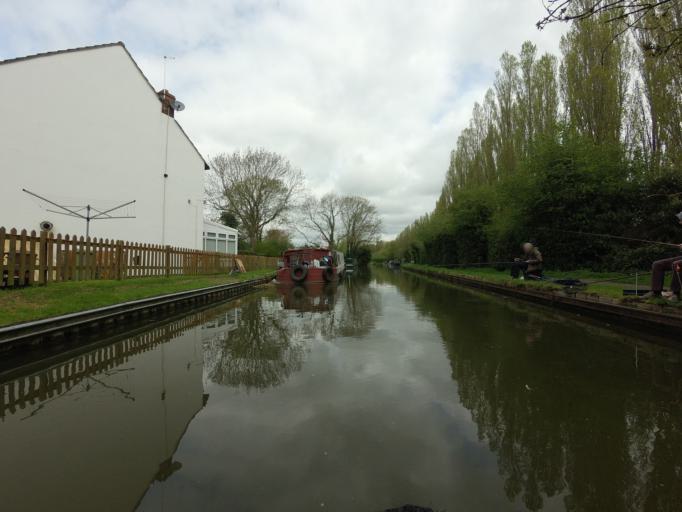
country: GB
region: England
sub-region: Milton Keynes
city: Water Eaton
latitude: 51.9882
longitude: -0.7173
